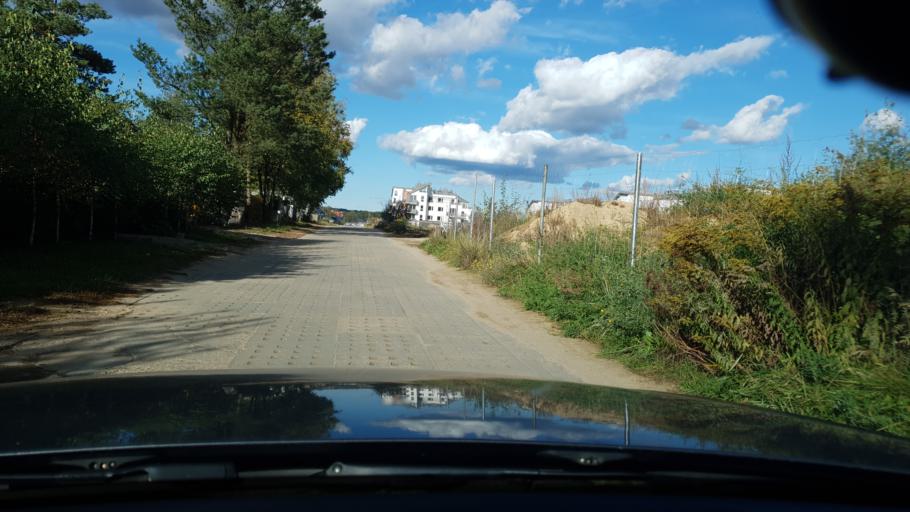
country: PL
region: Pomeranian Voivodeship
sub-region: Powiat wejherowski
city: Bojano
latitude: 54.4853
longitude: 18.4226
